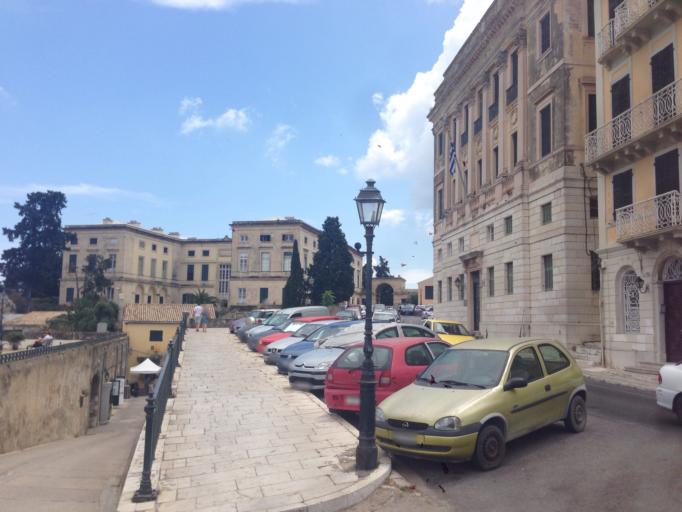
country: GR
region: Ionian Islands
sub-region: Nomos Kerkyras
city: Kerkyra
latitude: 39.6271
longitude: 19.9245
